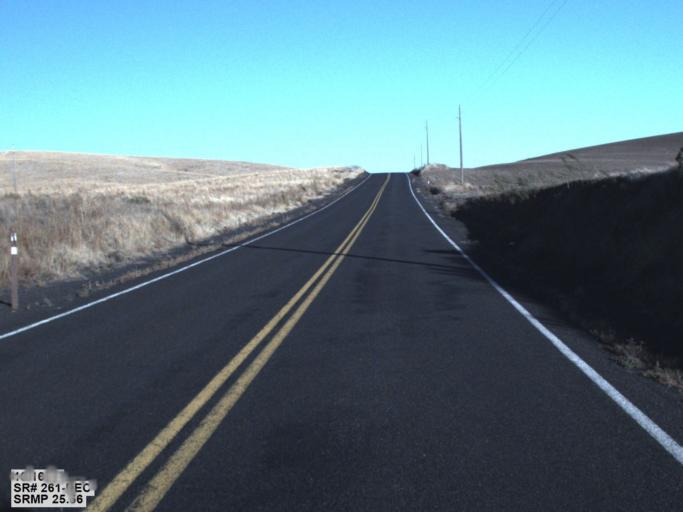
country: US
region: Washington
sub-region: Adams County
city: Ritzville
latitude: 46.6777
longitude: -118.3554
